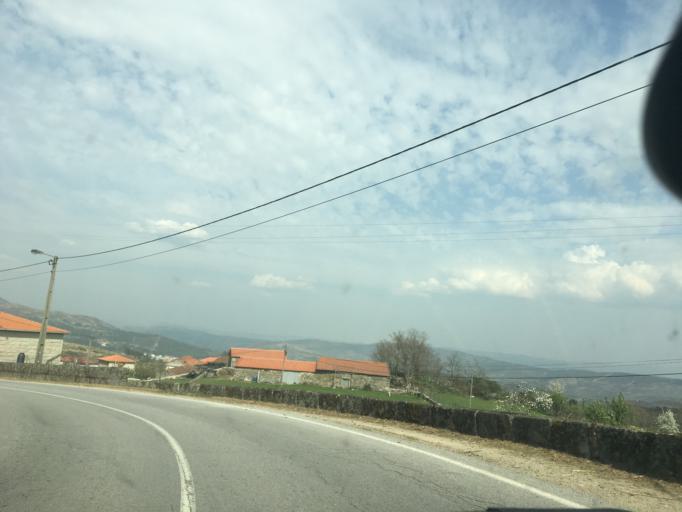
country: PT
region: Vila Real
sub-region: Boticas
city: Boticas
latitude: 41.6843
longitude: -7.6912
